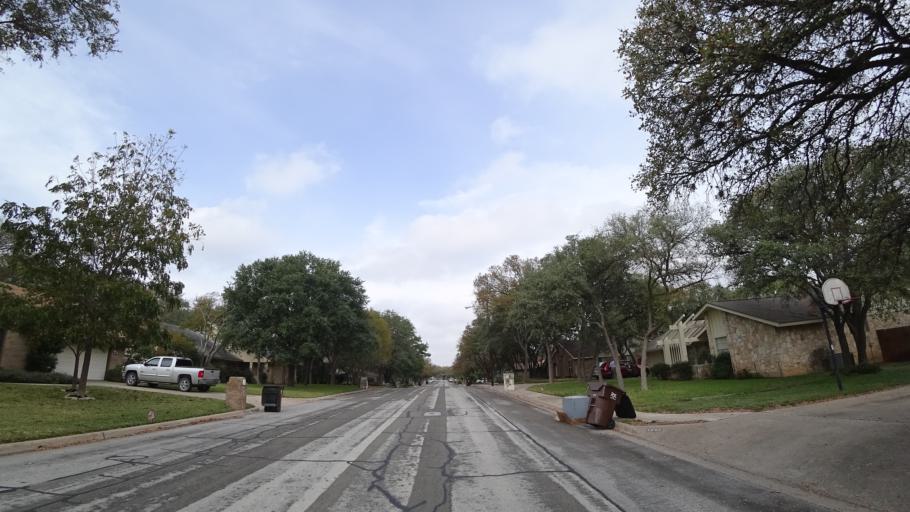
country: US
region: Texas
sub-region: Williamson County
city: Round Rock
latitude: 30.4972
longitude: -97.6908
